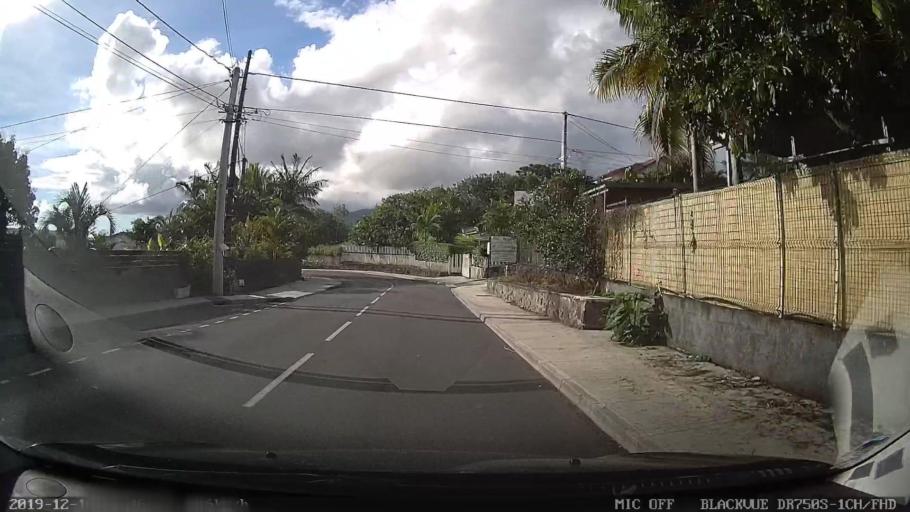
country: RE
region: Reunion
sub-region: Reunion
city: Le Tampon
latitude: -21.2465
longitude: 55.5171
